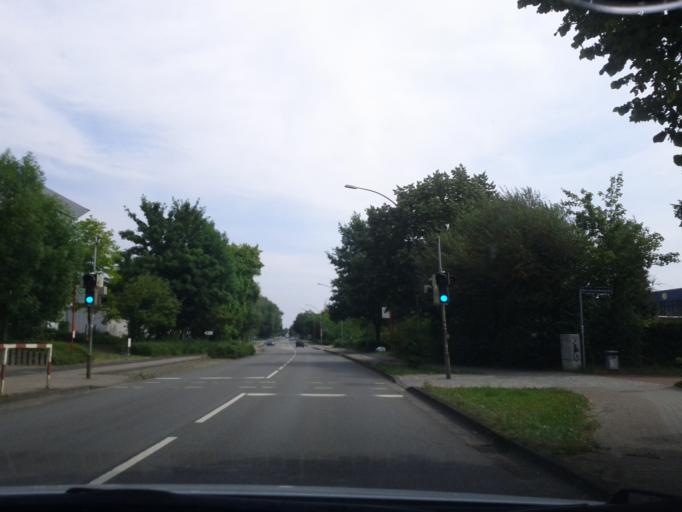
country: DE
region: Lower Saxony
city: Stade
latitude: 53.6062
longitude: 9.4664
